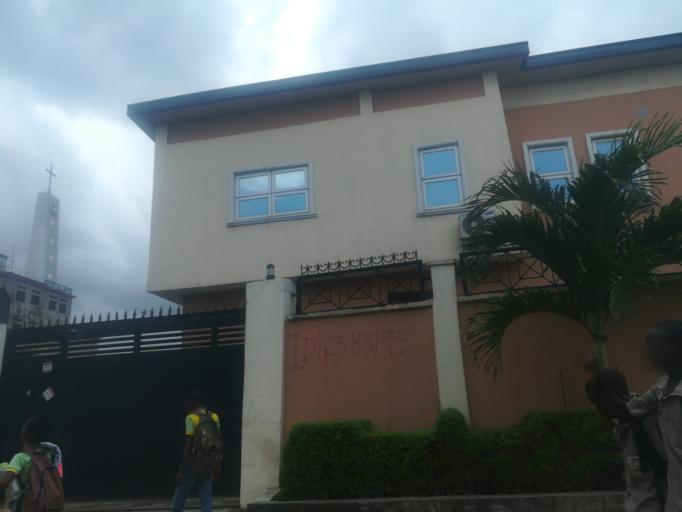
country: NG
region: Lagos
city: Ojota
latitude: 6.5657
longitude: 3.3891
